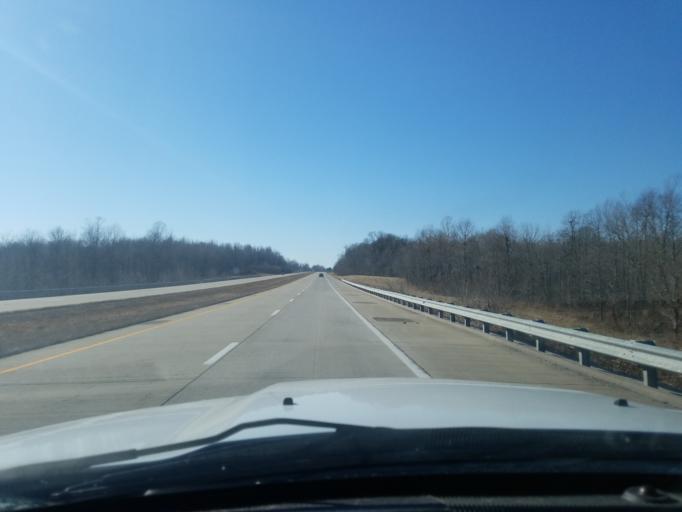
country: US
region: Indiana
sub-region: Warrick County
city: Newburgh
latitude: 37.7536
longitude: -87.3751
